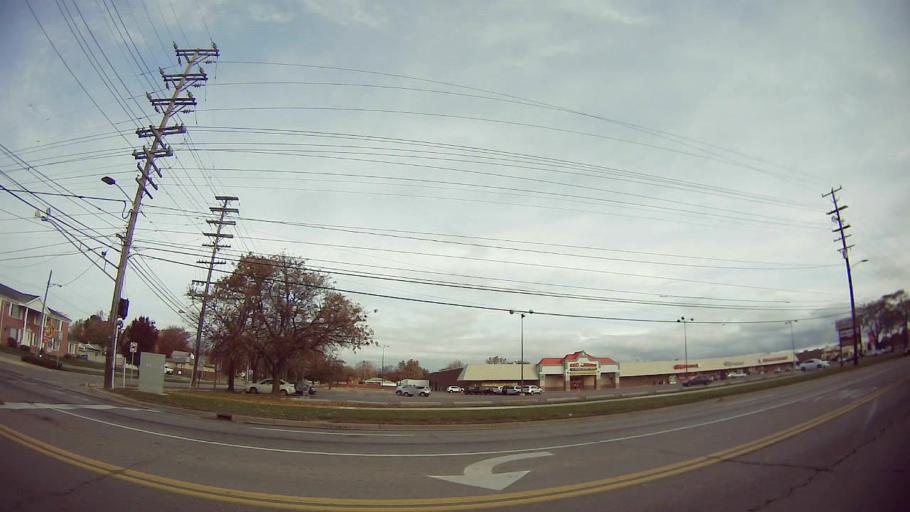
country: US
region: Michigan
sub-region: Macomb County
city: Warren
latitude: 42.4773
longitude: -83.0318
